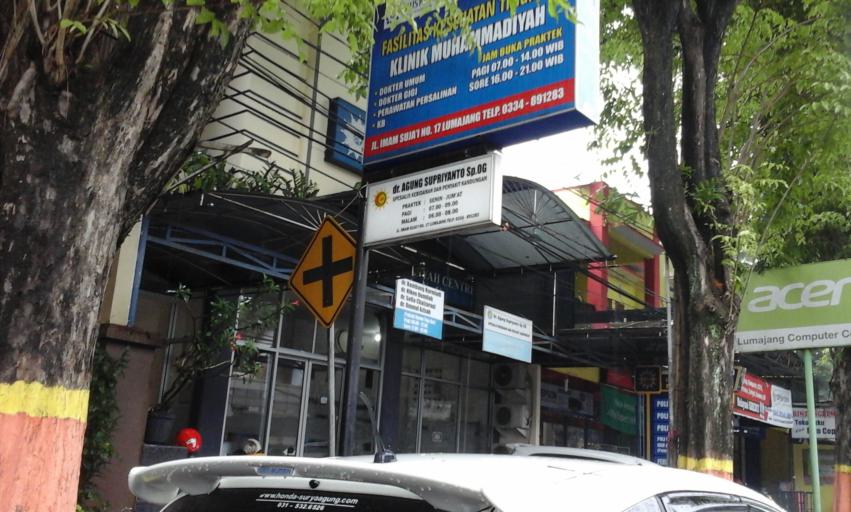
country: ID
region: East Java
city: Lumajang
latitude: -8.1373
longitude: 113.2246
